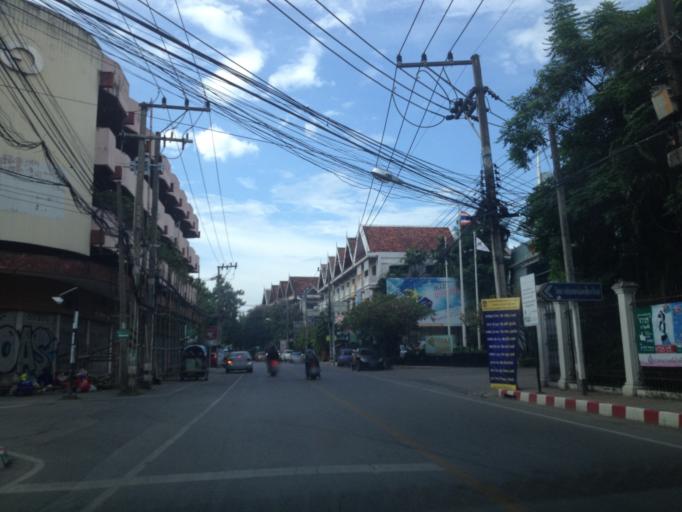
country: TH
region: Chiang Mai
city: Chiang Mai
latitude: 18.7929
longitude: 98.9876
